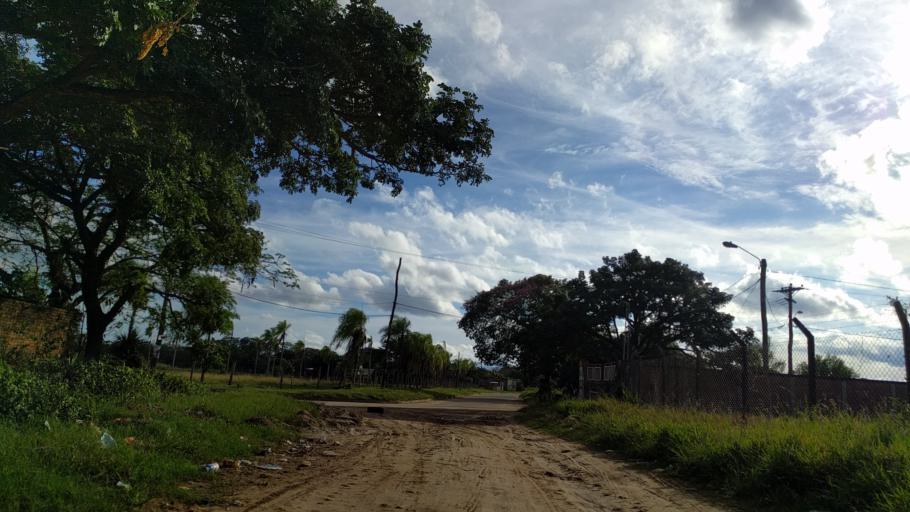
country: BO
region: Santa Cruz
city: Santa Cruz de la Sierra
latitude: -17.8553
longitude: -63.2686
